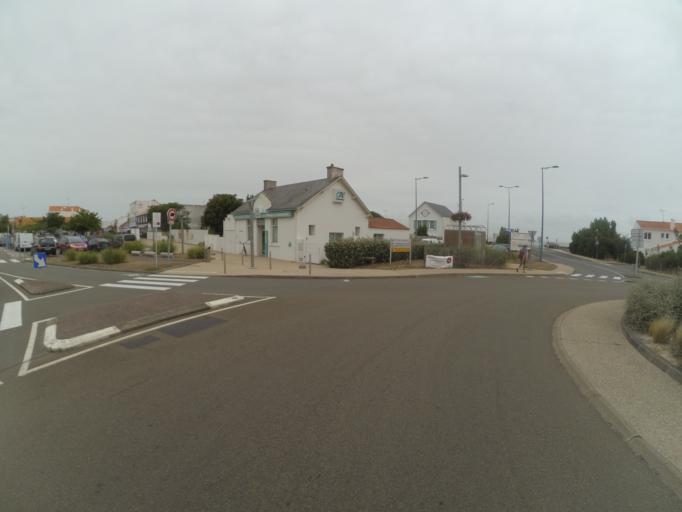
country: FR
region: Pays de la Loire
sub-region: Departement de la Vendee
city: La Barre-de-Monts
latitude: 46.8914
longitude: -2.1361
